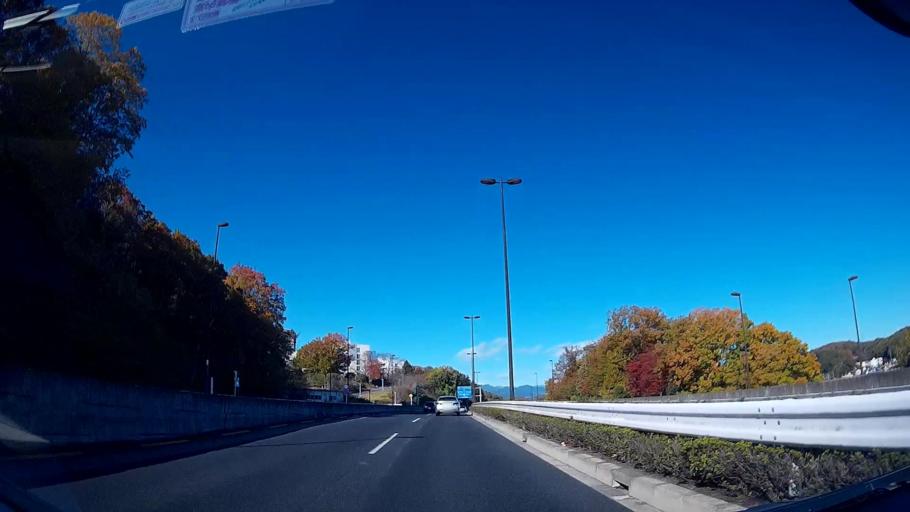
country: JP
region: Tokyo
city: Hachioji
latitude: 35.6933
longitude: 139.3262
